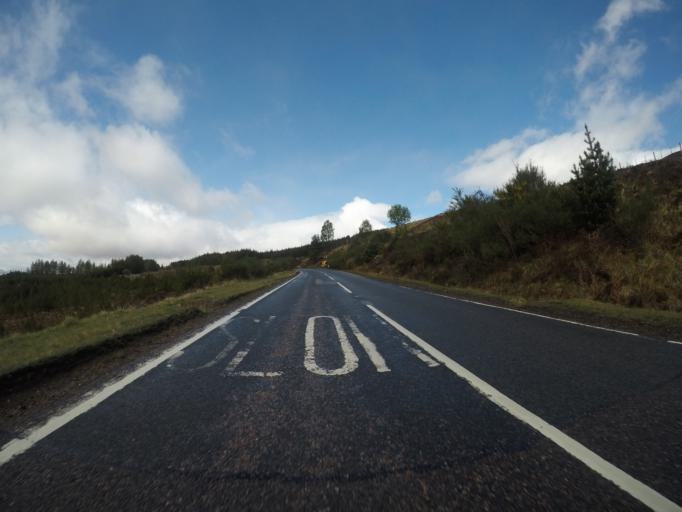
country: GB
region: Scotland
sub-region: Highland
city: Spean Bridge
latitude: 57.0873
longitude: -4.9660
